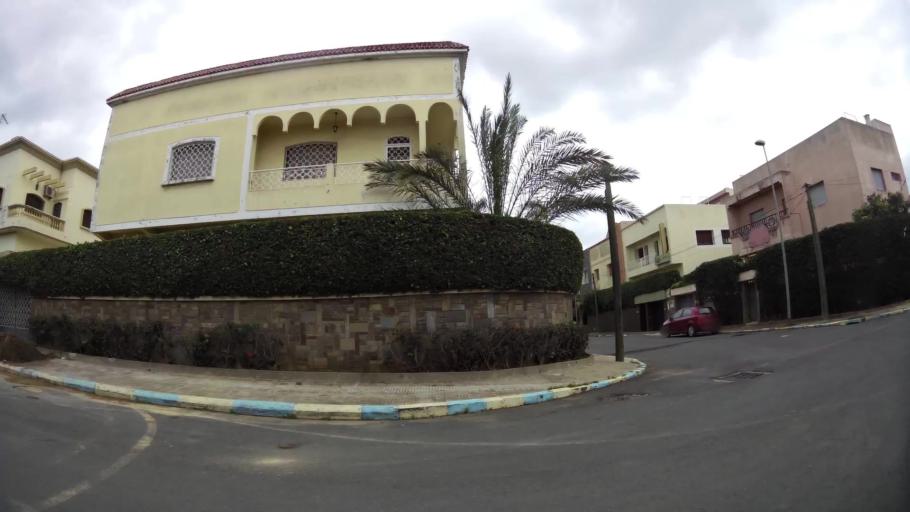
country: MA
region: Grand Casablanca
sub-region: Casablanca
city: Casablanca
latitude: 33.5571
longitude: -7.6095
